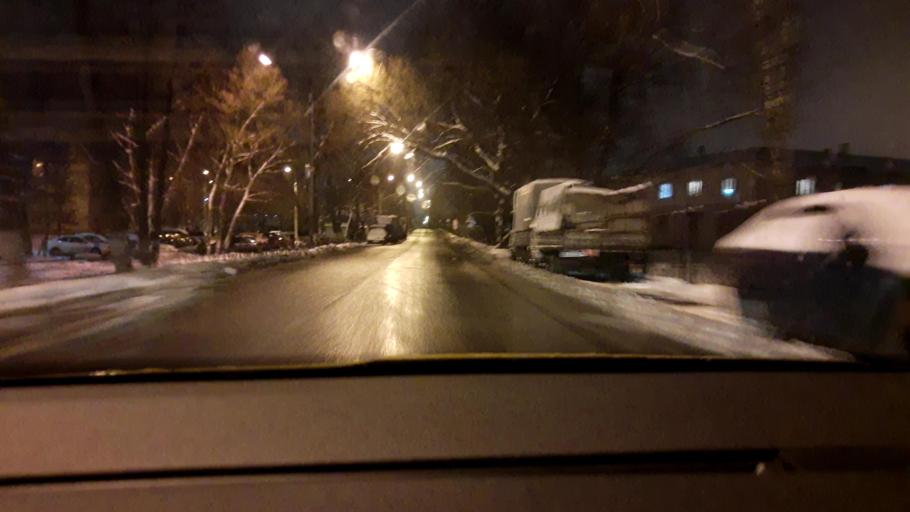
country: RU
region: Moskovskaya
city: Biryulevo Zapadnoye
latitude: 55.5651
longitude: 37.6426
